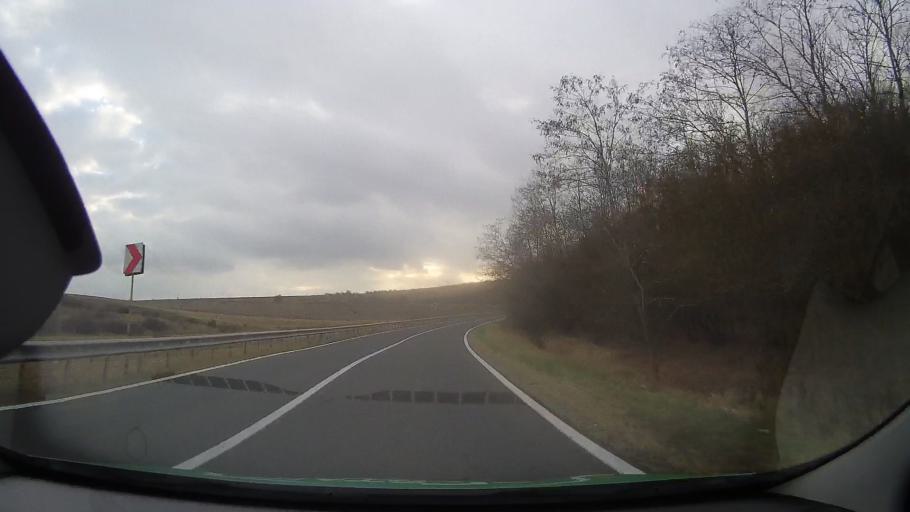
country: RO
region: Constanta
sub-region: Comuna Deleni
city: Deleni
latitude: 44.1002
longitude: 28.0222
